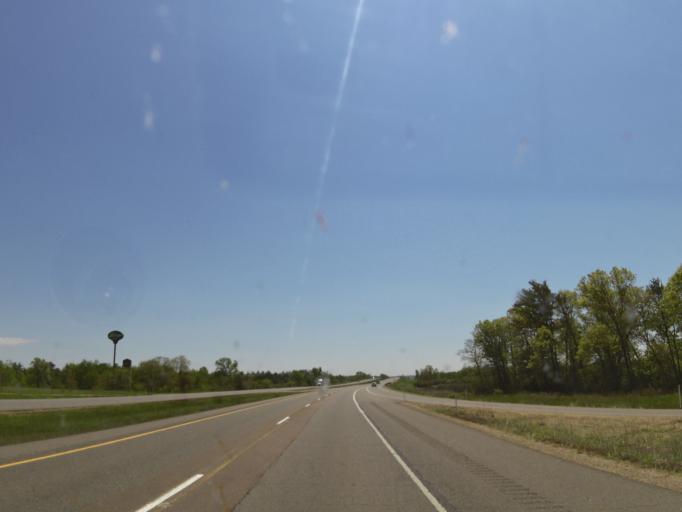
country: US
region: Wisconsin
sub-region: Monroe County
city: Tomah
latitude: 44.0176
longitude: -90.4957
